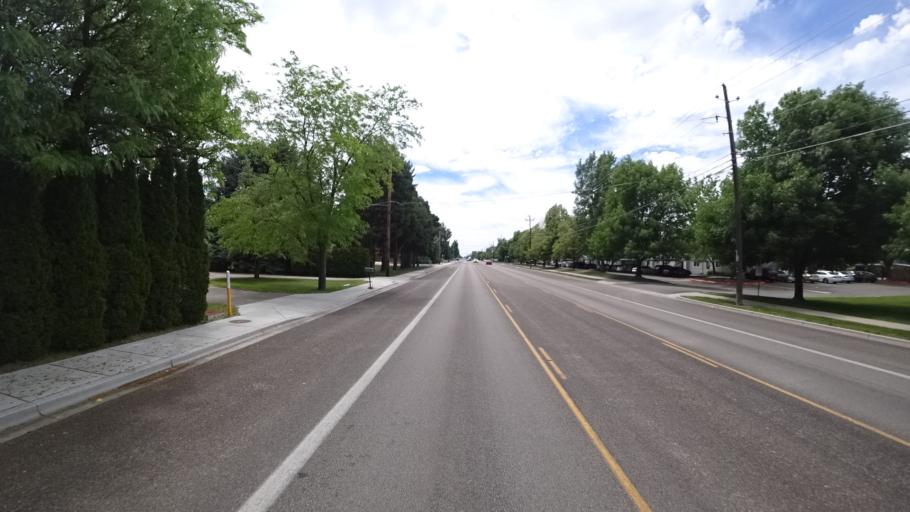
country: US
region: Idaho
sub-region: Ada County
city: Eagle
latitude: 43.6374
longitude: -116.3143
